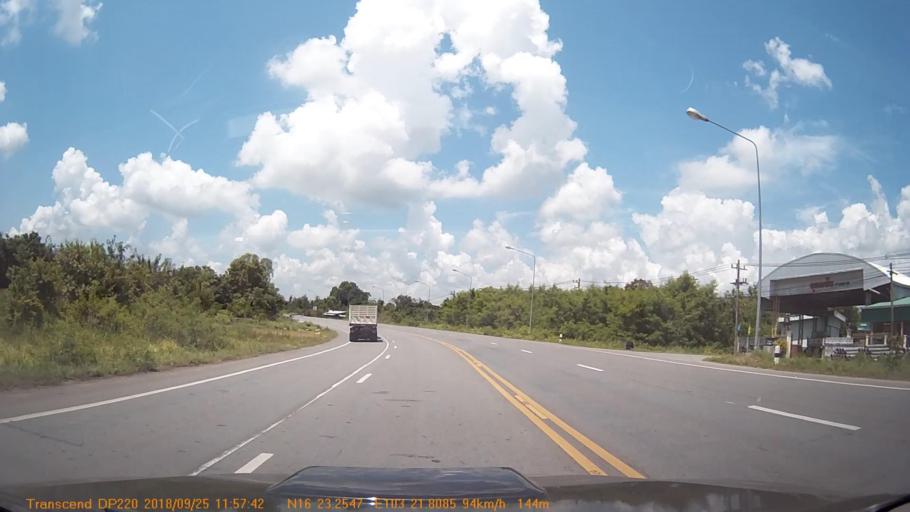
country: TH
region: Kalasin
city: Yang Talat
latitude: 16.3878
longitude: 103.3633
